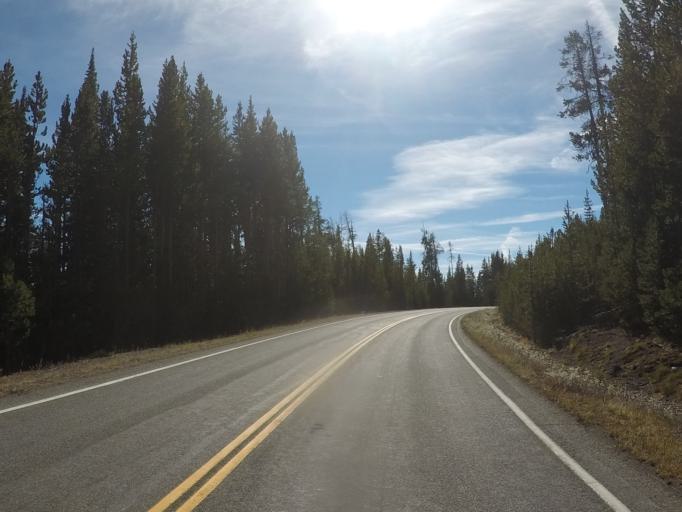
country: US
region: Montana
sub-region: Gallatin County
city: West Yellowstone
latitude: 44.4205
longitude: -110.5918
